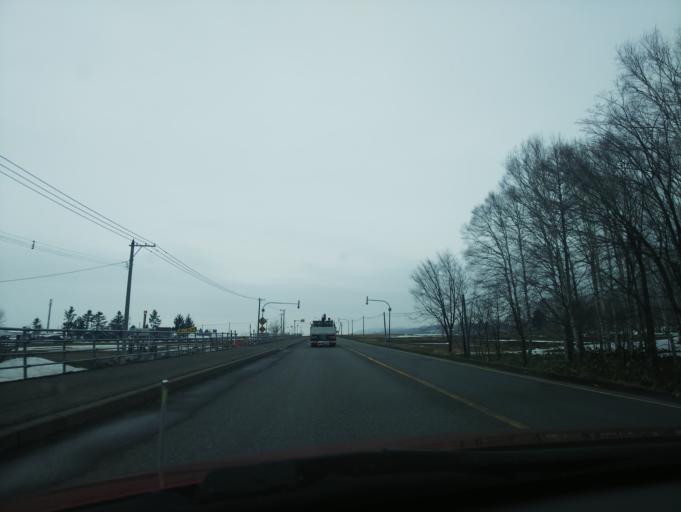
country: JP
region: Hokkaido
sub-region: Asahikawa-shi
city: Asahikawa
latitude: 44.0605
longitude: 142.4030
